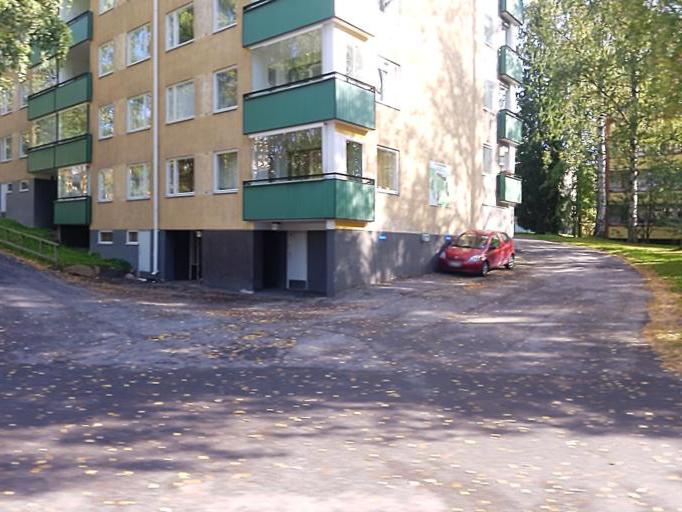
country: FI
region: Uusimaa
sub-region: Helsinki
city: Teekkarikylae
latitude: 60.2425
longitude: 24.8789
